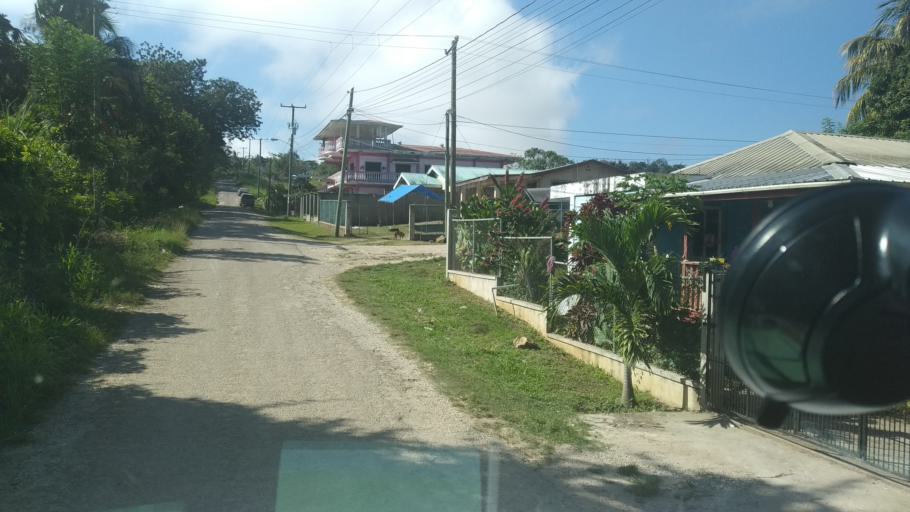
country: BZ
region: Cayo
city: Benque Viejo del Carmen
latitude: 17.0839
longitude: -89.1323
